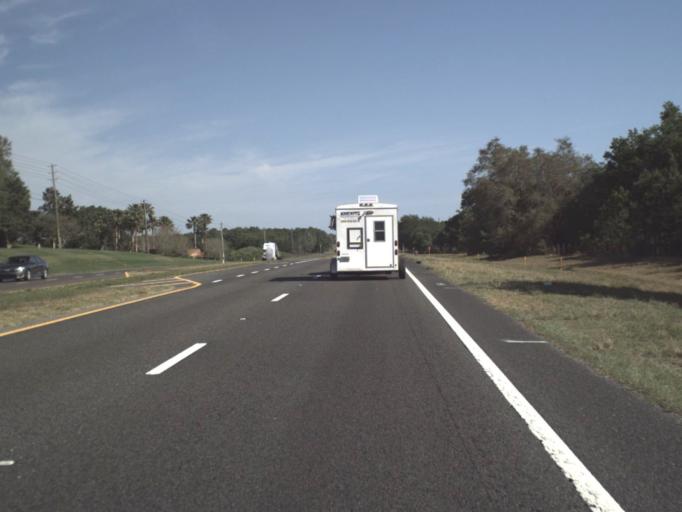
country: US
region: Florida
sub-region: Lake County
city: Yalaha
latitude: 28.6973
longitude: -81.8571
